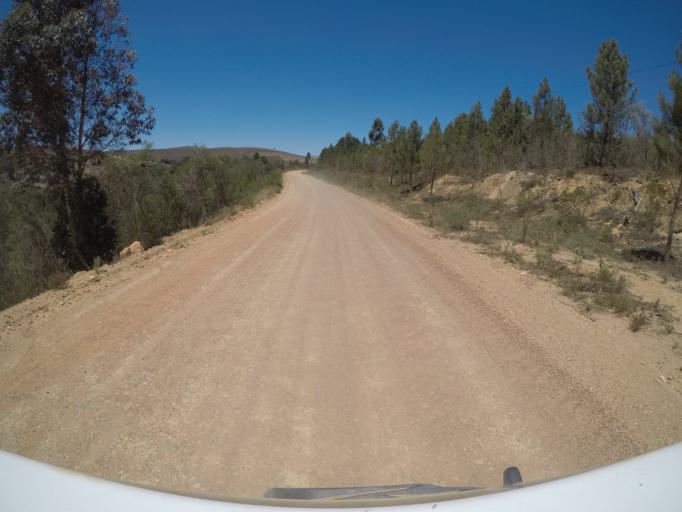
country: ZA
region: Western Cape
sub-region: Overberg District Municipality
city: Caledon
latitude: -34.1858
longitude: 19.2235
